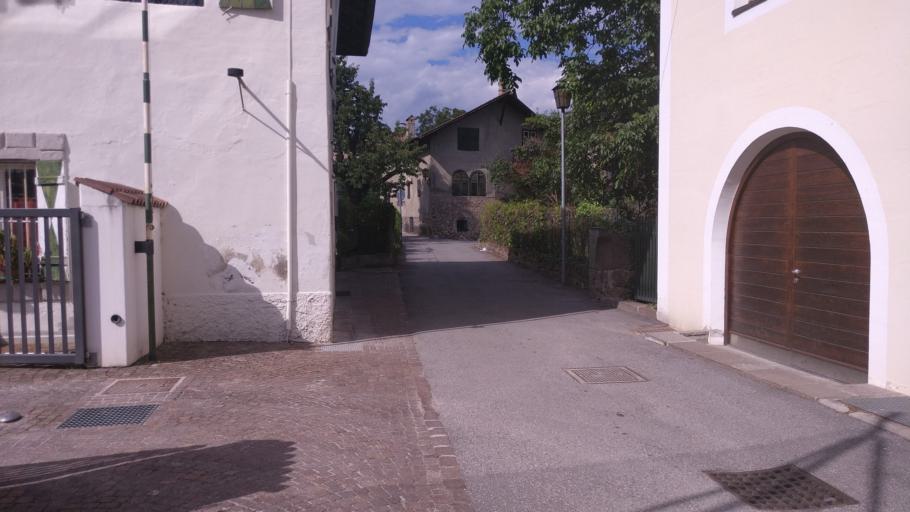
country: IT
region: Trentino-Alto Adige
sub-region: Bolzano
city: San Michele
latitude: 46.4562
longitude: 11.2565
